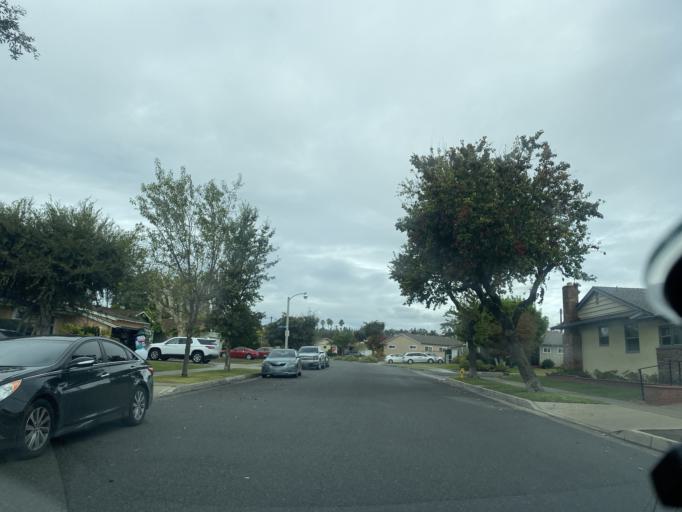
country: US
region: California
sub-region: Orange County
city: Fullerton
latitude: 33.8752
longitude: -117.9026
